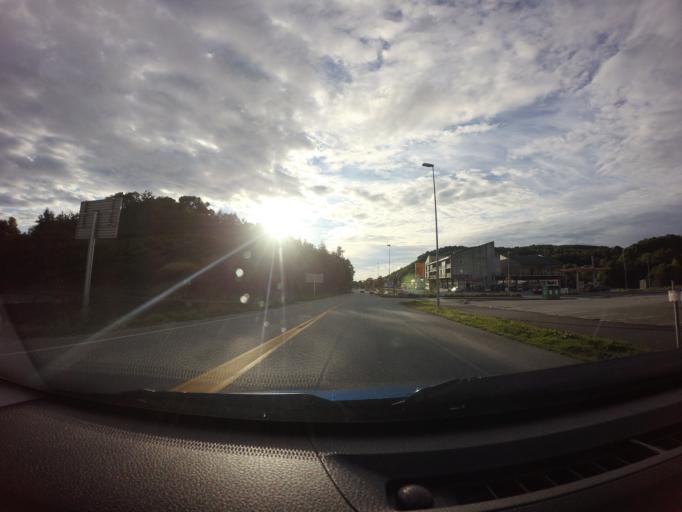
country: NO
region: Rogaland
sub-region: Strand
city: Tau
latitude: 59.0648
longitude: 5.9204
